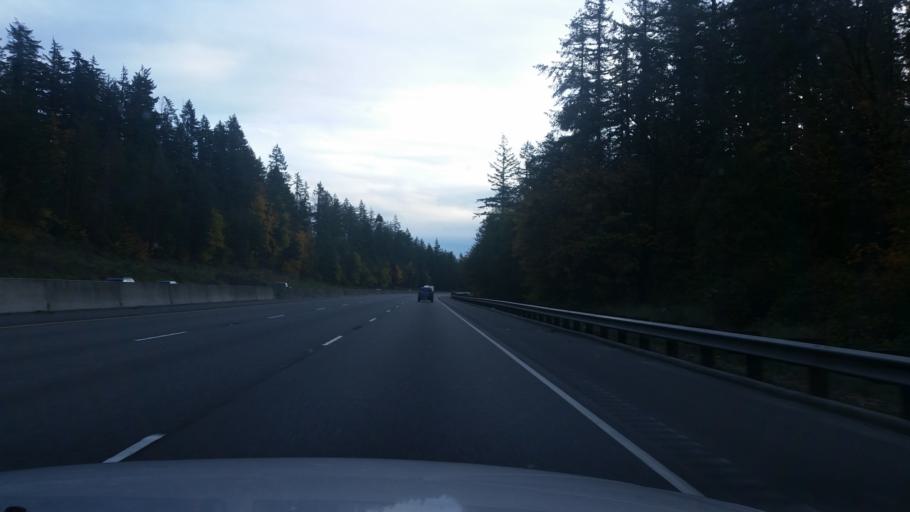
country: US
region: Washington
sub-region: Thurston County
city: Grand Mound
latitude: 46.8627
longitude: -122.9719
